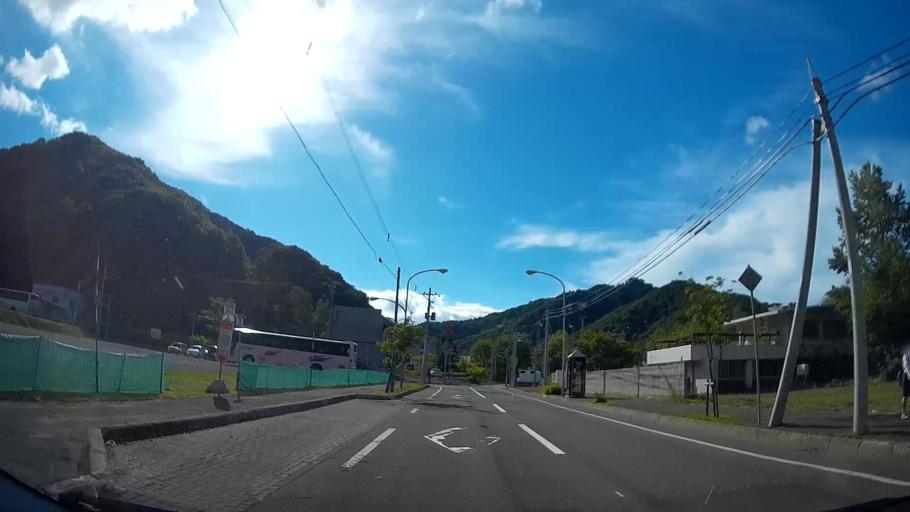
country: JP
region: Hokkaido
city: Sapporo
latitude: 42.9697
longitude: 141.1648
